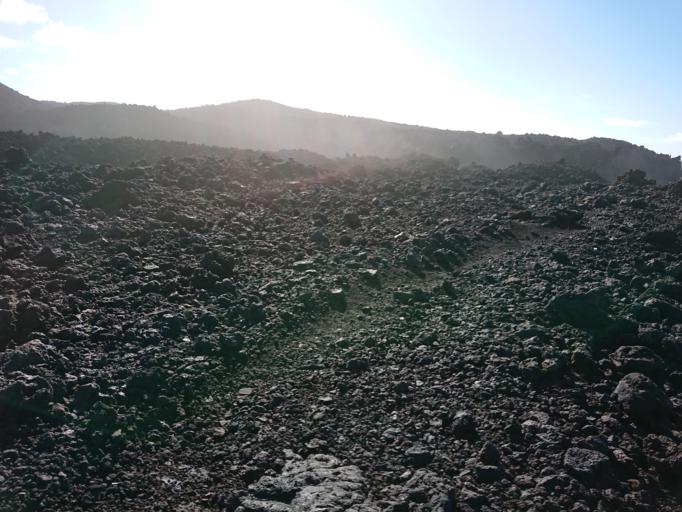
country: ES
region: Canary Islands
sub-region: Provincia de Las Palmas
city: Tinajo
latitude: 29.0807
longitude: -13.7344
